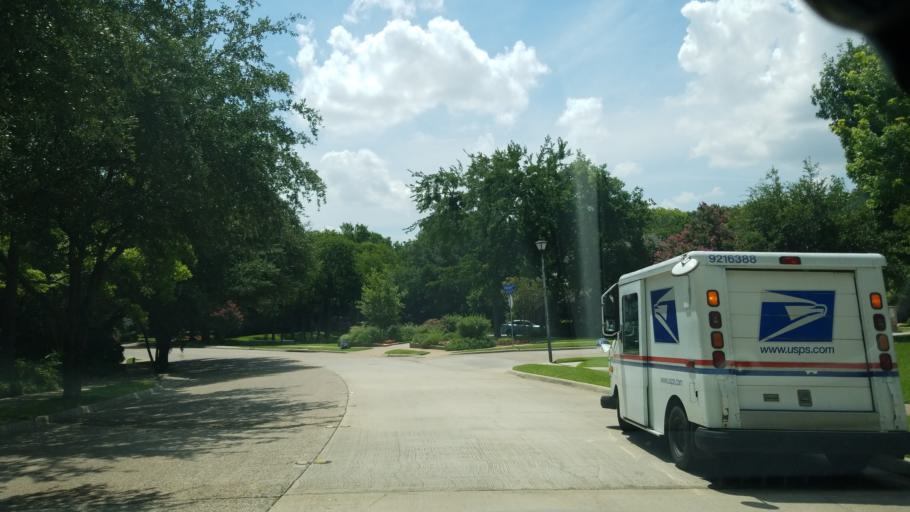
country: US
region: Texas
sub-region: Dallas County
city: Coppell
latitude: 32.9591
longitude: -96.9742
